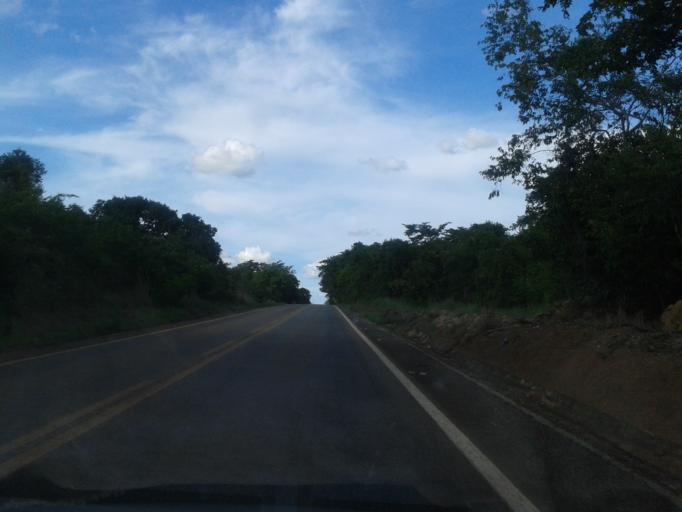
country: BR
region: Goias
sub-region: Mozarlandia
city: Mozarlandia
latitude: -14.4312
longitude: -50.4548
